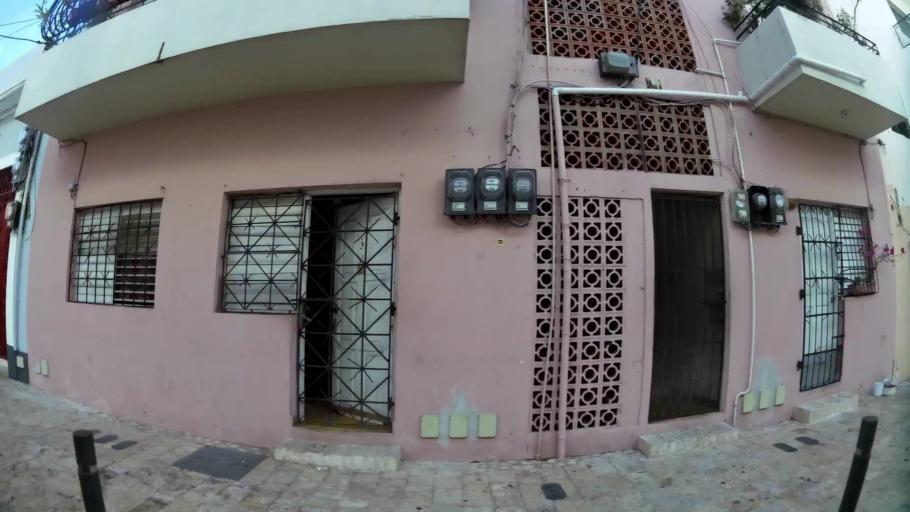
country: DO
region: Nacional
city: Ciudad Nueva
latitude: 18.4709
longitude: -69.8841
